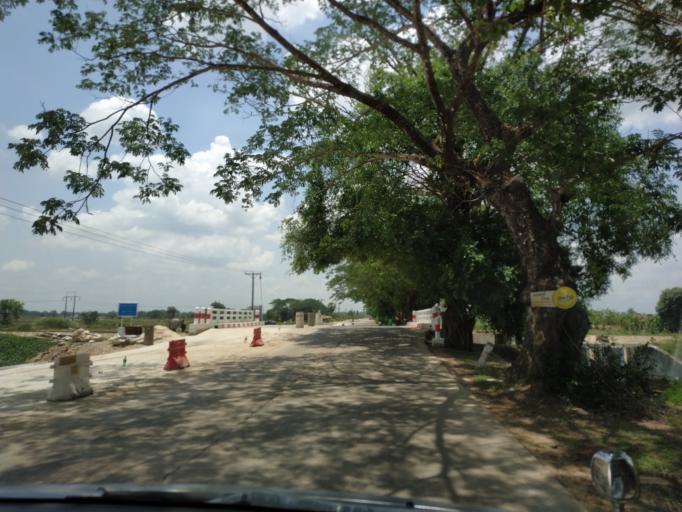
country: MM
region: Bago
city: Bago
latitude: 17.4787
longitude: 96.4952
